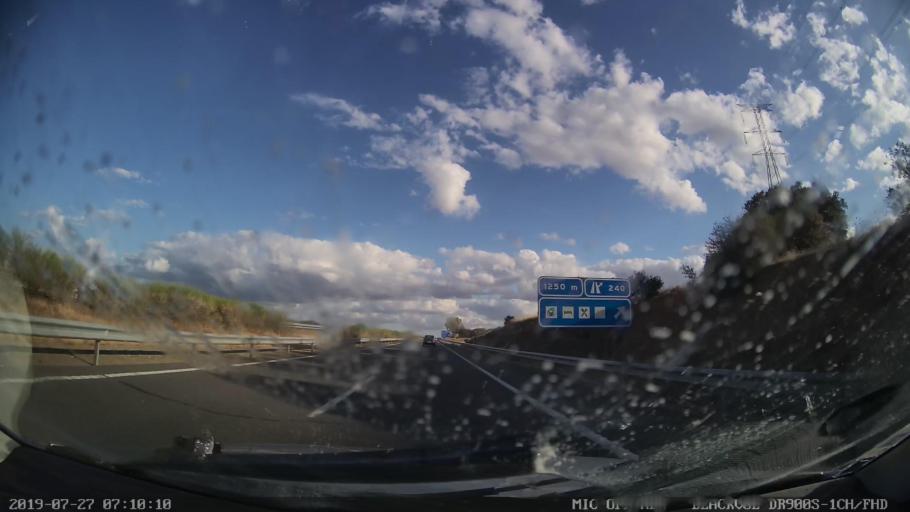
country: ES
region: Extremadura
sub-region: Provincia de Caceres
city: Jaraicejo
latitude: 39.5802
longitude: -5.8348
